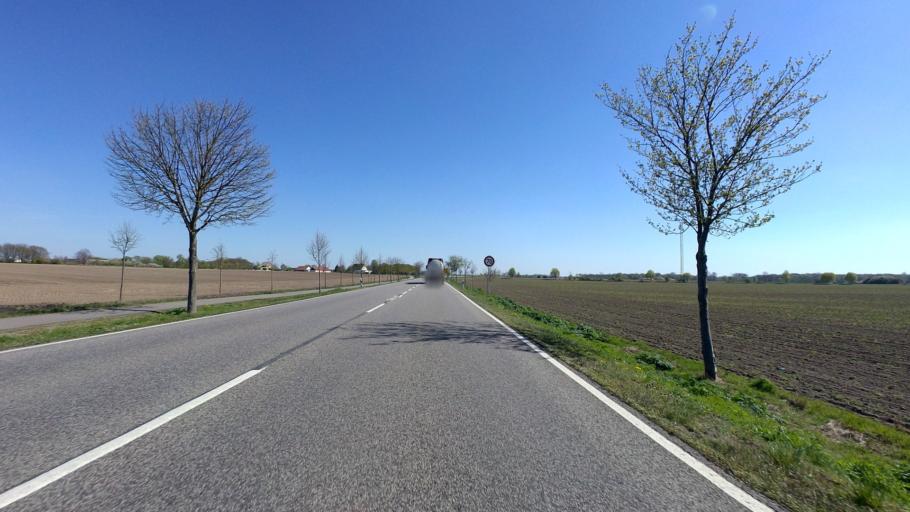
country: DE
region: Saxony-Anhalt
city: Pretzier
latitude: 52.8148
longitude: 11.2154
